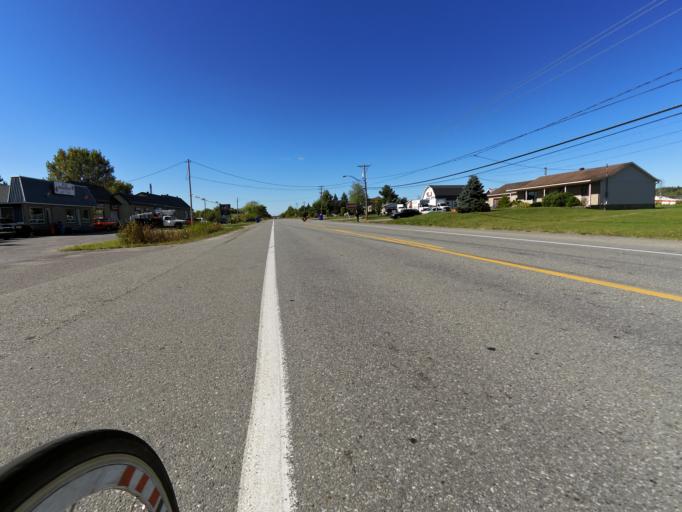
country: CA
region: Ontario
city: Clarence-Rockland
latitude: 45.5372
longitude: -75.4442
